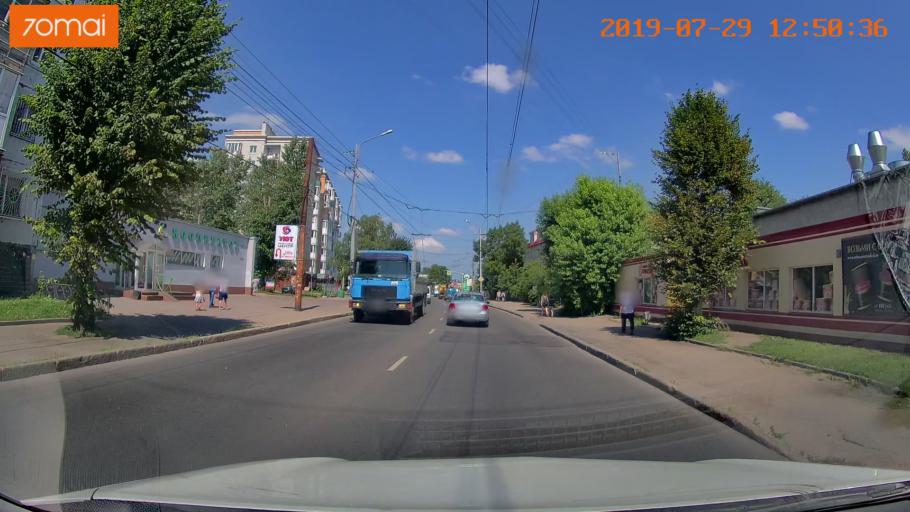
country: RU
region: Kaliningrad
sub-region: Gorod Kaliningrad
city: Kaliningrad
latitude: 54.6879
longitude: 20.5326
